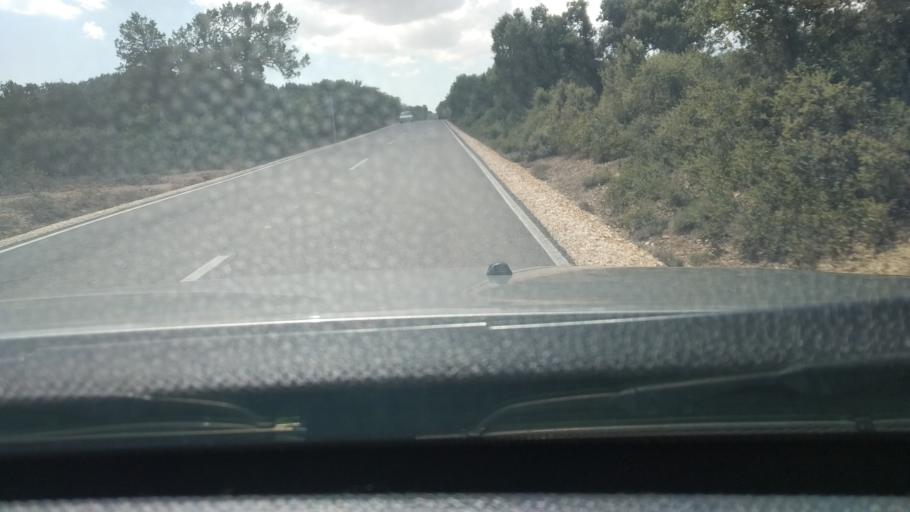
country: ES
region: Castille and Leon
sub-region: Provincia de Burgos
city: Avellanosa de Muno
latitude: 41.9684
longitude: -3.8130
